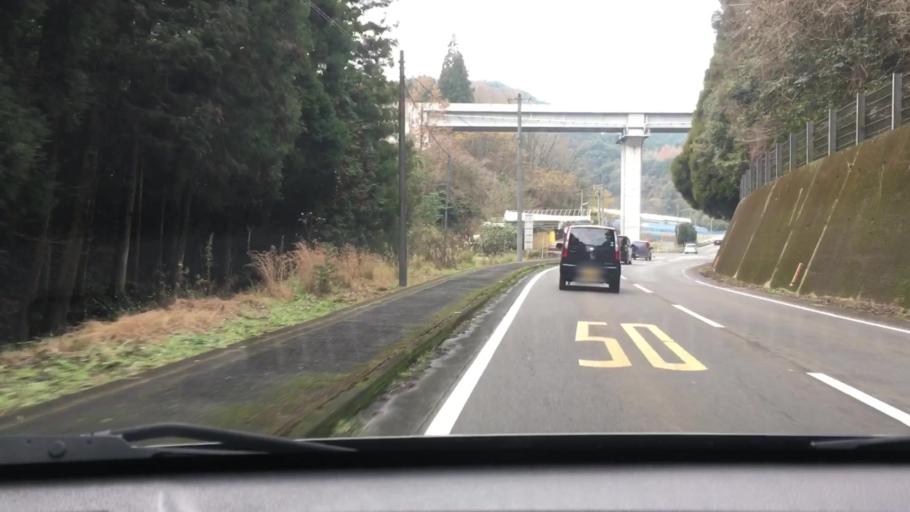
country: JP
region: Saga Prefecture
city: Imaricho-ko
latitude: 33.3391
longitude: 129.9256
